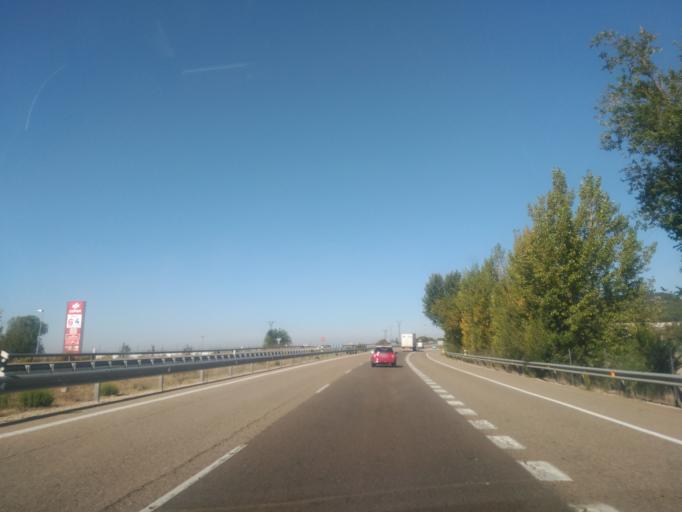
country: ES
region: Castille and Leon
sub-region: Provincia de Valladolid
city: Cisterniga
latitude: 41.5987
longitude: -4.6549
